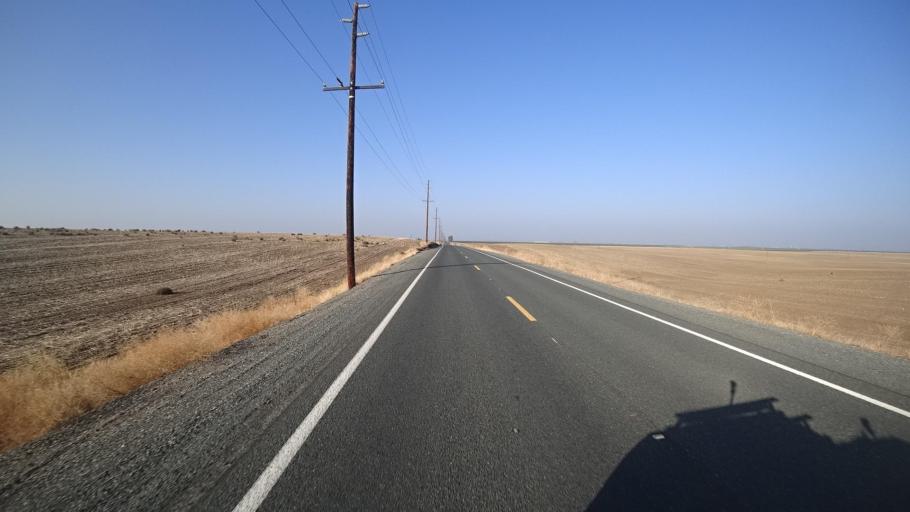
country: US
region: California
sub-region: Tulare County
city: Richgrove
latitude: 35.7619
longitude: -119.0685
